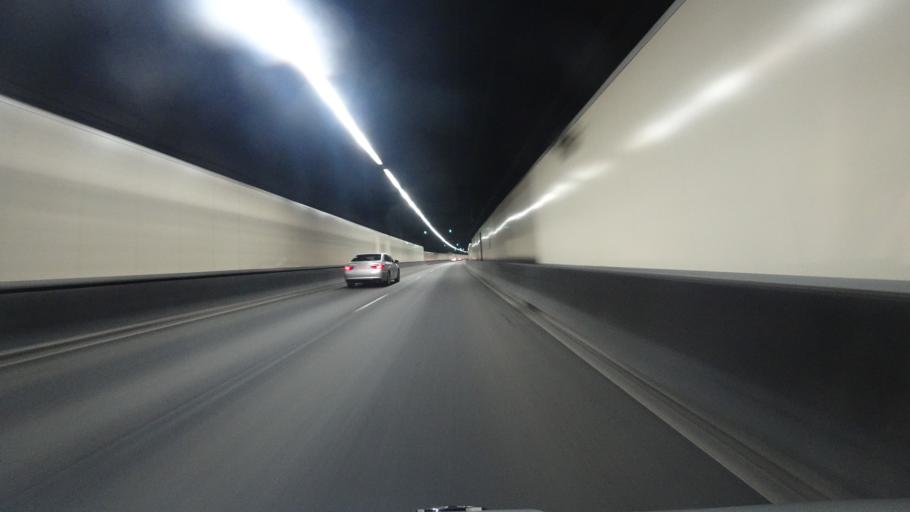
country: AU
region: New South Wales
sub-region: Rockdale
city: Bardwell Valley
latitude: -33.9371
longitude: 151.1336
